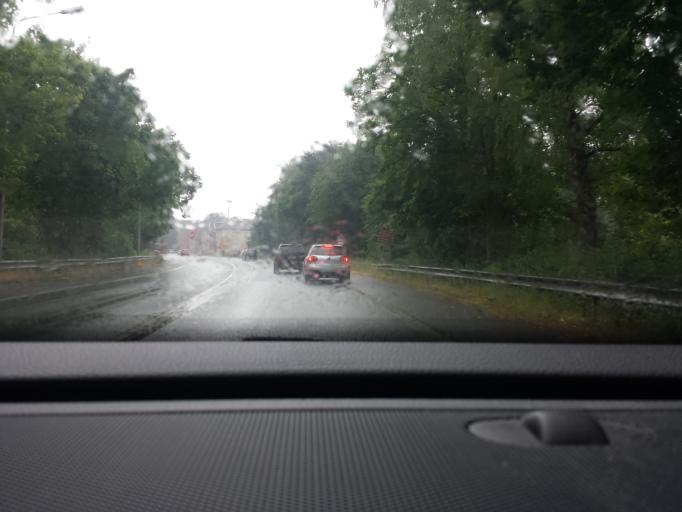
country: DE
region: North Rhine-Westphalia
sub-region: Regierungsbezirk Munster
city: Gronau
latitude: 52.2081
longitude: 7.0255
